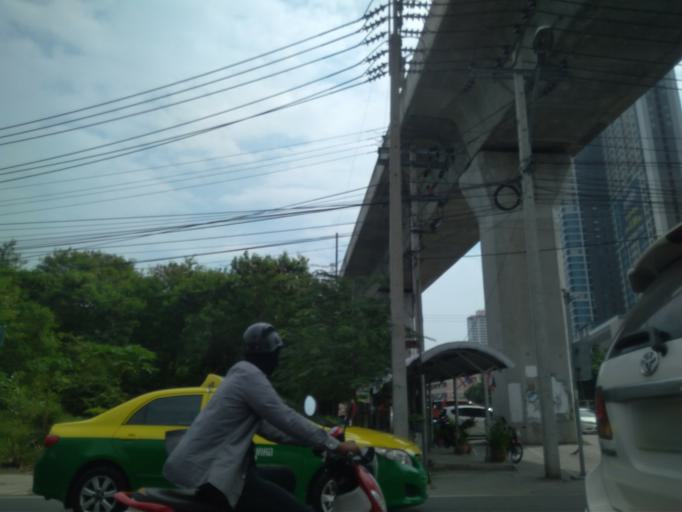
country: TH
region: Bangkok
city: Suan Luang
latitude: 13.7385
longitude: 100.6418
